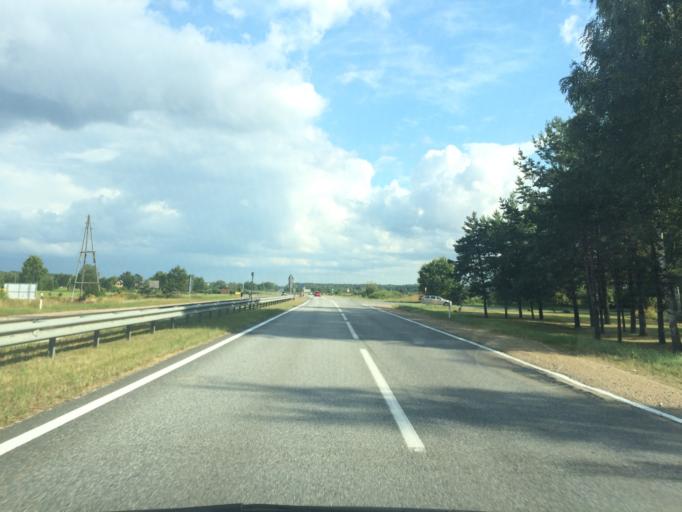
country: LV
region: Ikskile
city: Ikskile
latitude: 56.8238
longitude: 24.5320
